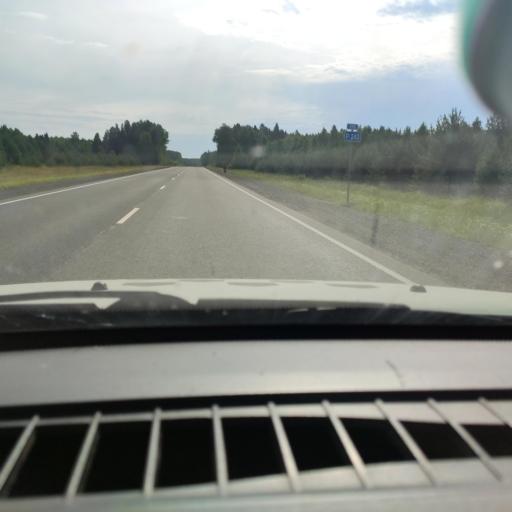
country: RU
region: Perm
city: Siva
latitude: 58.3847
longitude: 54.5853
